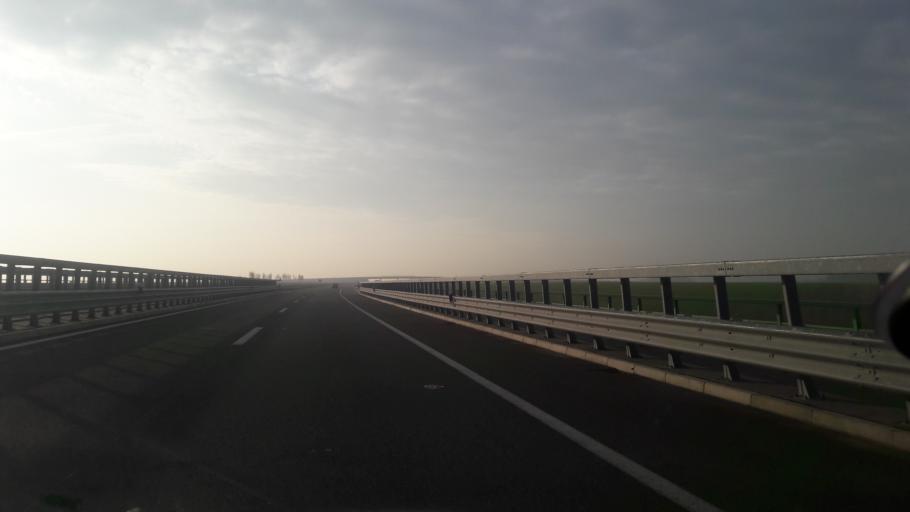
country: HR
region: Osjecko-Baranjska
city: Gorjani
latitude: 45.3579
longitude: 18.4000
